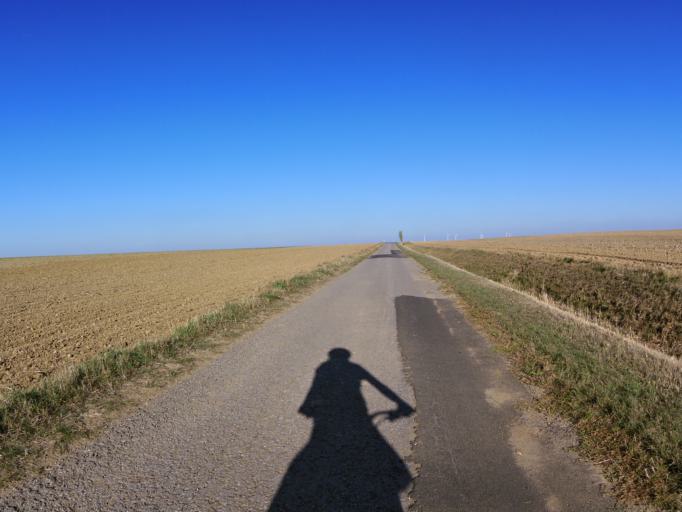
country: DE
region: Bavaria
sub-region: Regierungsbezirk Unterfranken
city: Eibelstadt
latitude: 49.7032
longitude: 9.9872
